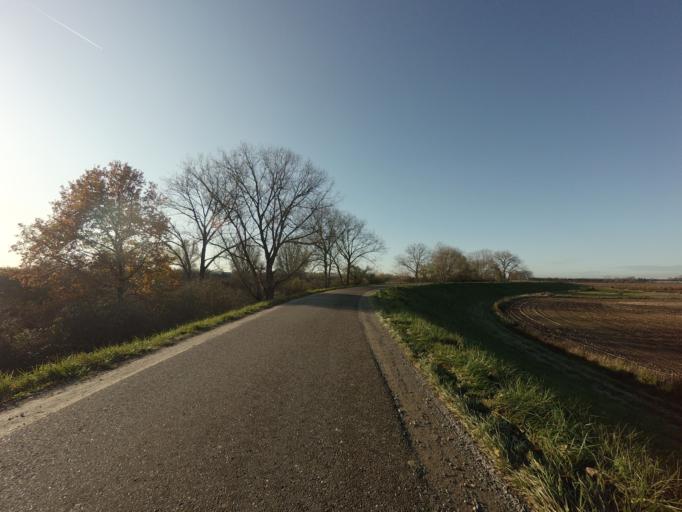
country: NL
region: Gelderland
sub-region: Gemeente Maasdriel
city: Hedel
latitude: 51.7460
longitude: 5.3036
